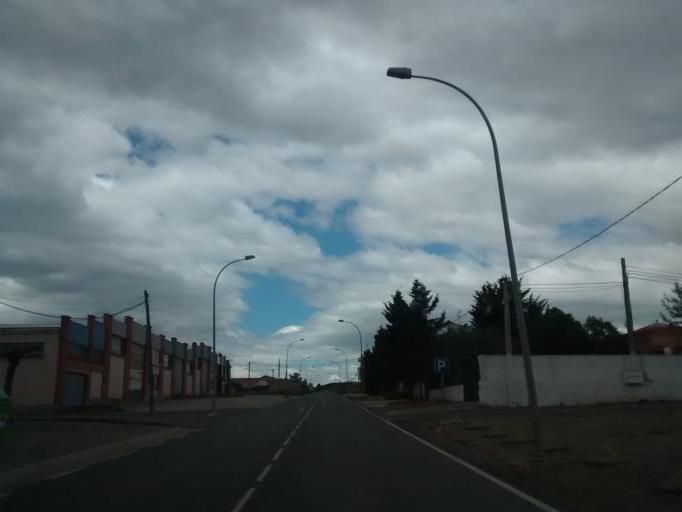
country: ES
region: La Rioja
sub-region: Provincia de La Rioja
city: Pradejon
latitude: 42.3363
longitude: -2.0746
